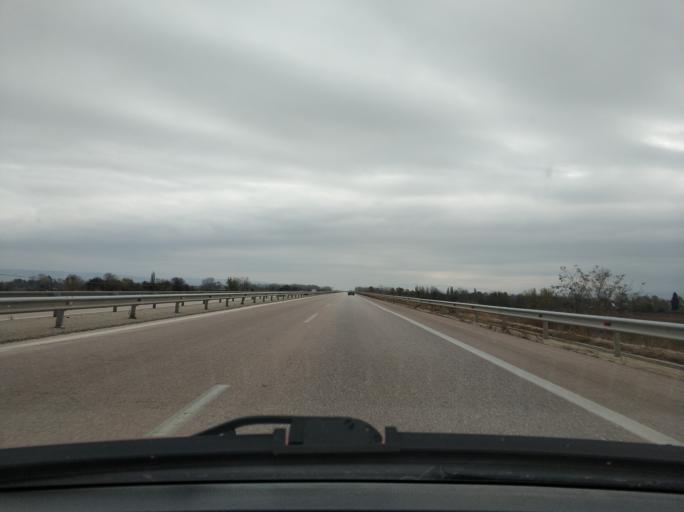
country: GR
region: Central Macedonia
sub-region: Nomos Thessalonikis
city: Kavallari
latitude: 40.7339
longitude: 23.0426
